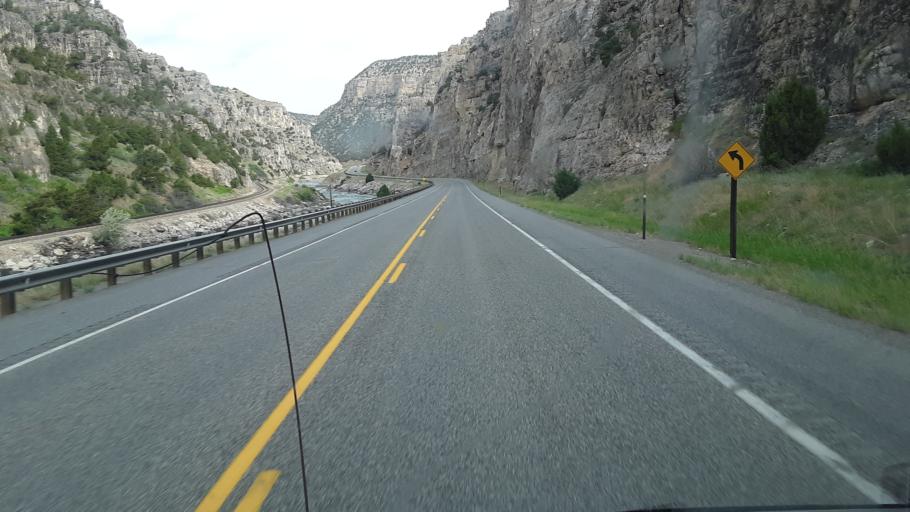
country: US
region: Wyoming
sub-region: Hot Springs County
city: Thermopolis
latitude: 43.5417
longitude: -108.1825
